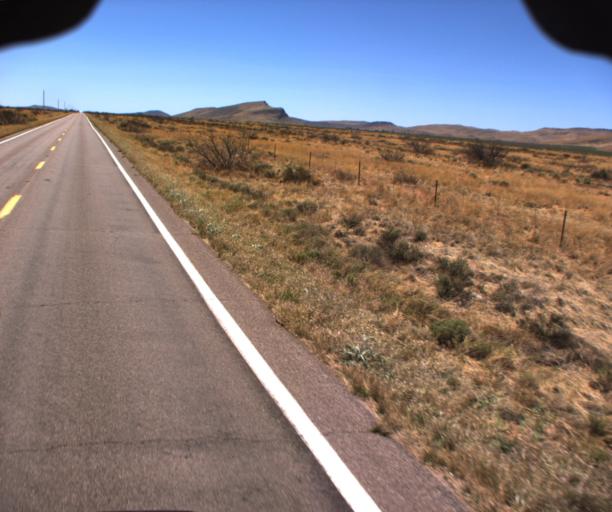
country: US
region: Arizona
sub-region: Cochise County
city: Douglas
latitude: 31.7128
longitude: -109.1174
